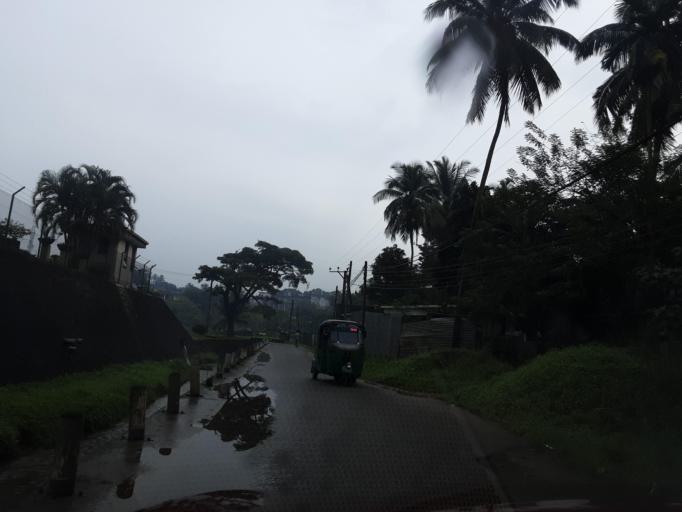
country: LK
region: Central
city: Kandy
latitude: 7.3193
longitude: 80.6228
